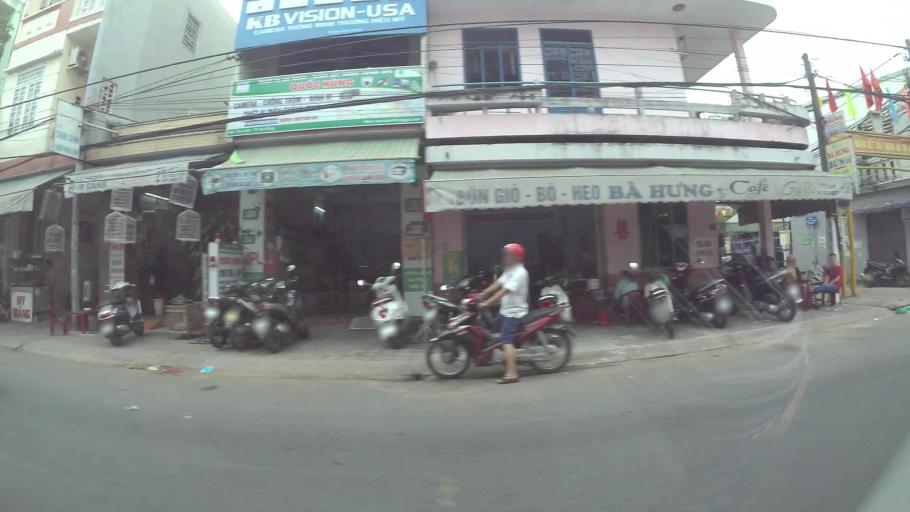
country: VN
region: Da Nang
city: Thanh Khe
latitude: 16.0686
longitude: 108.2016
